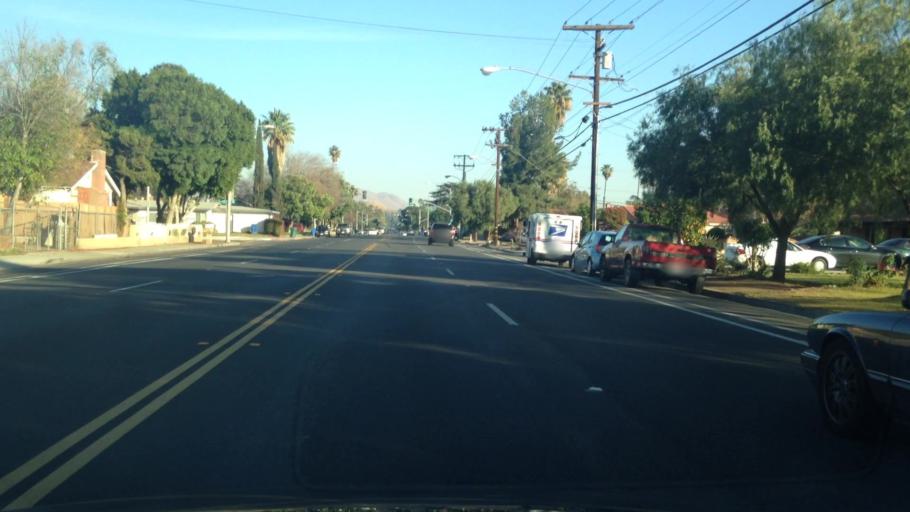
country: US
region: California
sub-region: Riverside County
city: Riverside
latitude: 33.9621
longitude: -117.4204
